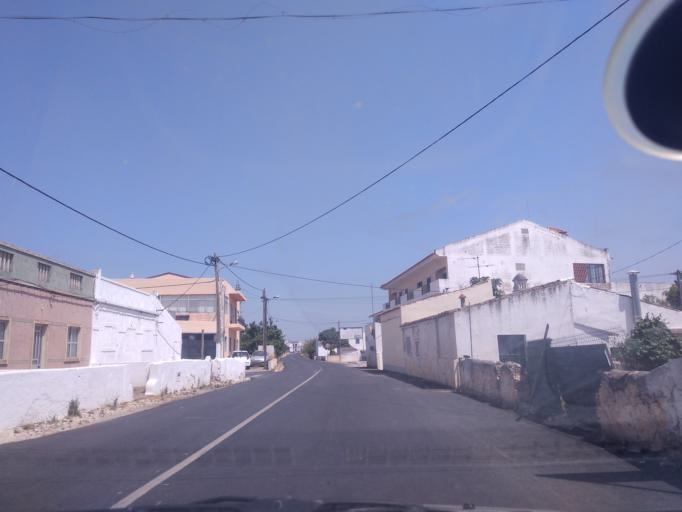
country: PT
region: Faro
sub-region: Faro
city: Faro
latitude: 37.0517
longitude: -7.9420
